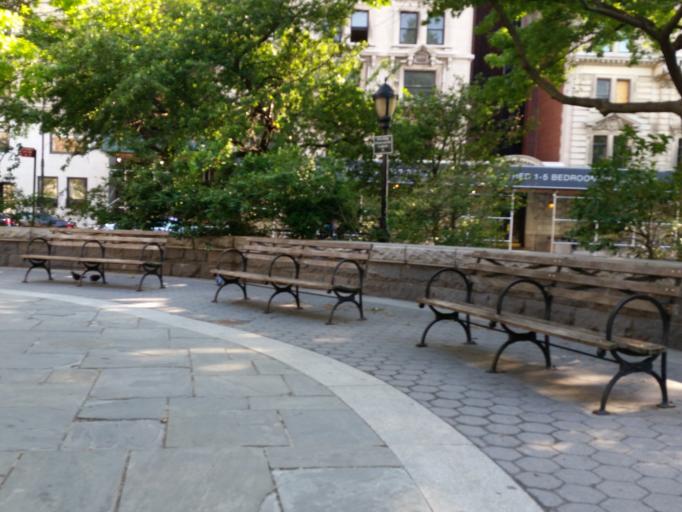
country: US
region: New York
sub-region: New York County
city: Manhattan
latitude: 40.7808
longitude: -73.9859
